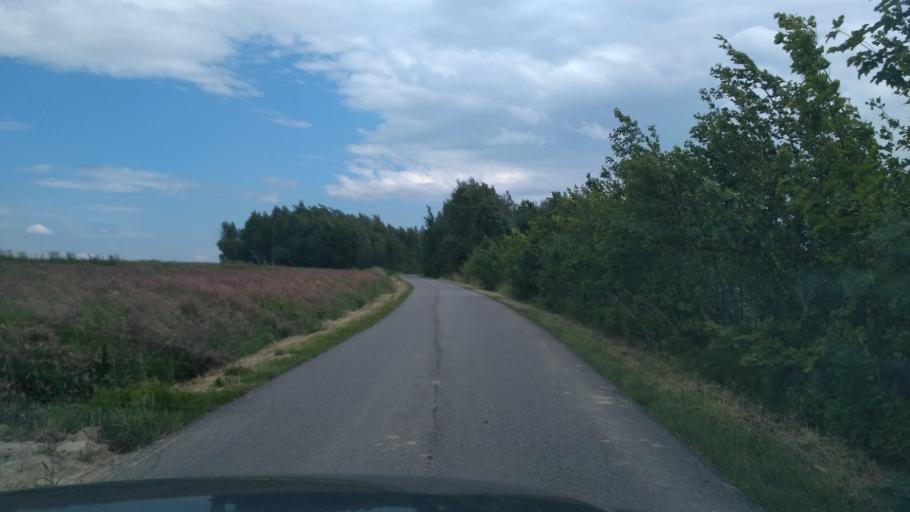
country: PL
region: Subcarpathian Voivodeship
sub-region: Powiat ropczycko-sedziszowski
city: Wielopole Skrzynskie
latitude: 49.9733
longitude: 21.6353
